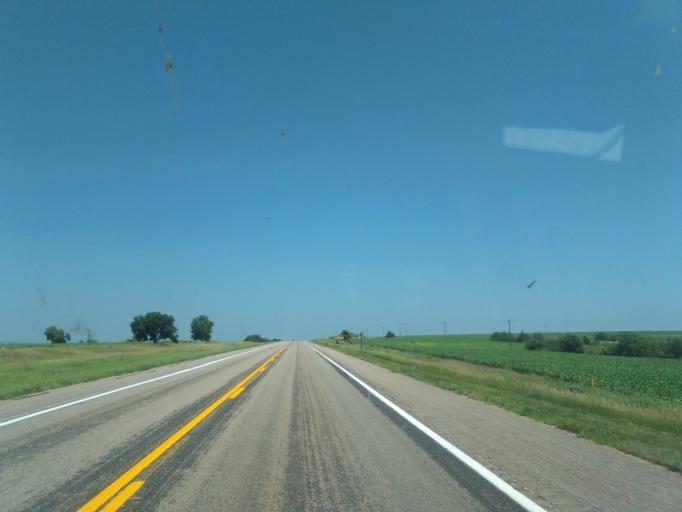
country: US
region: Nebraska
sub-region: Frontier County
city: Stockville
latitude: 40.5999
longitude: -100.6296
